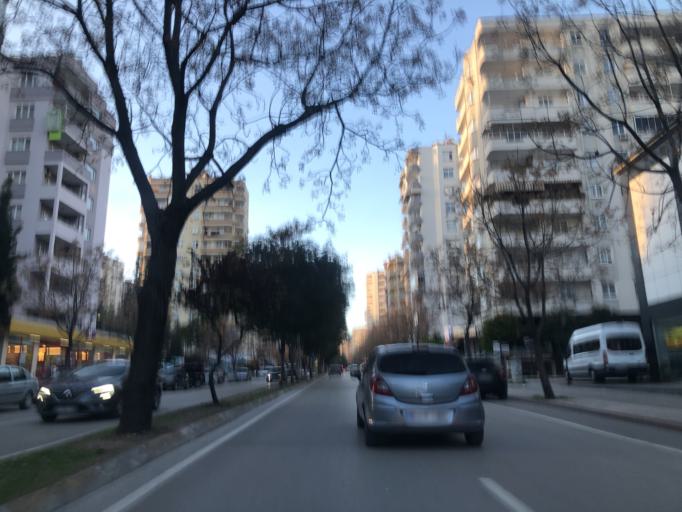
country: TR
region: Adana
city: Adana
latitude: 37.0441
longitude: 35.2981
